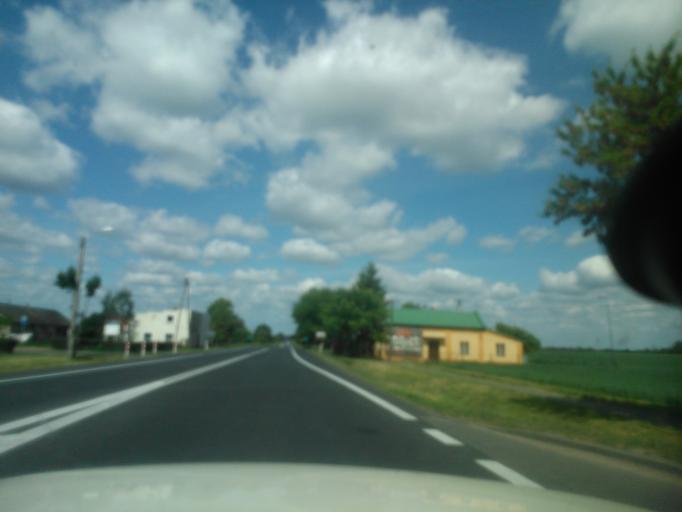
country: PL
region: Kujawsko-Pomorskie
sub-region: Powiat torunski
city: Obrowo
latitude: 53.0084
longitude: 18.8347
